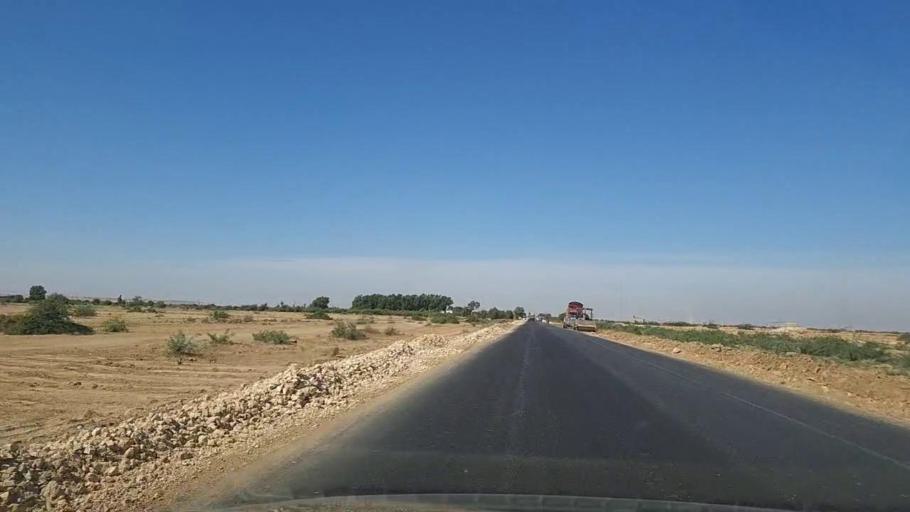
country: PK
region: Sindh
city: Kotri
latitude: 25.2600
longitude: 68.2229
